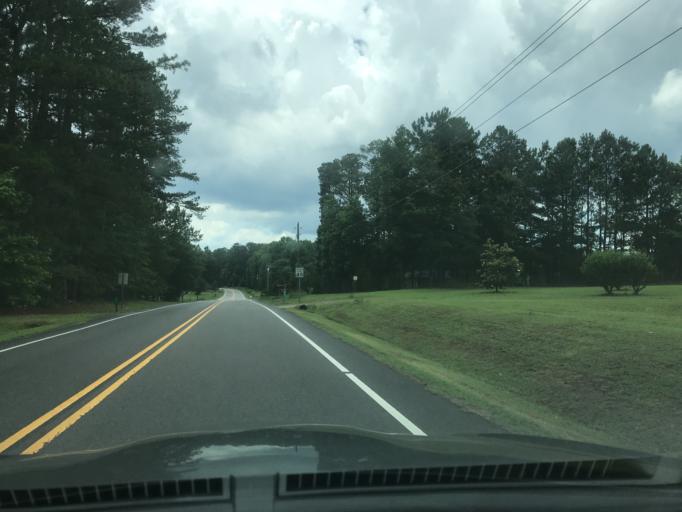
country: US
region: North Carolina
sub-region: Wake County
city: Knightdale
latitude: 35.8351
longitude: -78.4737
